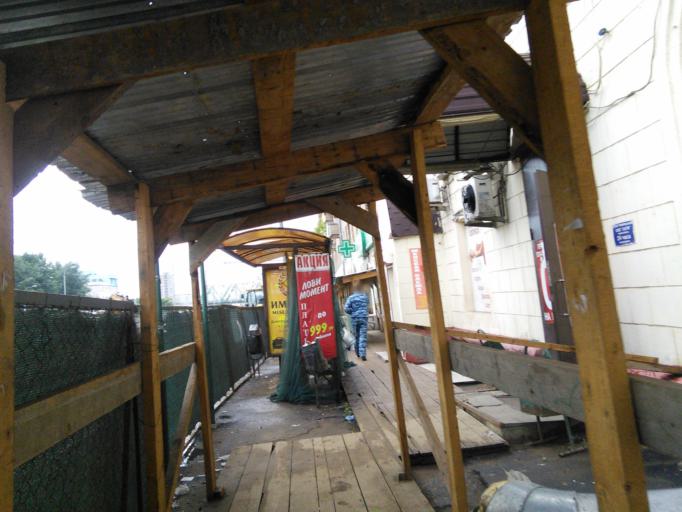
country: RU
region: Moscow
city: Likhobory
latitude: 55.8464
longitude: 37.5687
